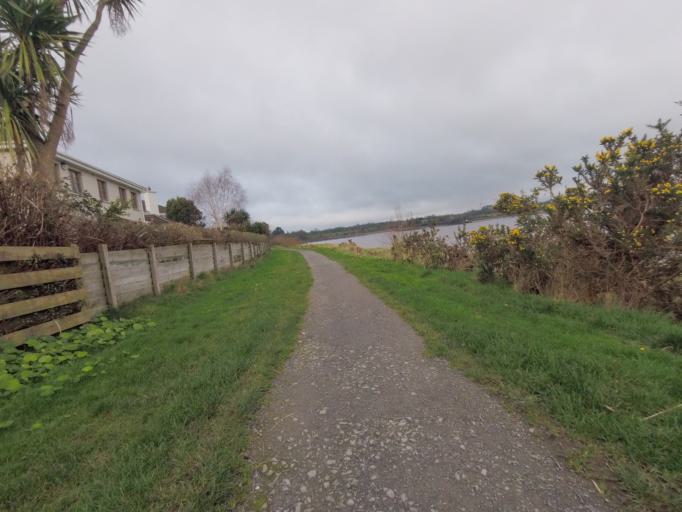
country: IE
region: Munster
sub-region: Waterford
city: Waterford
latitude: 52.2527
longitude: -7.0676
